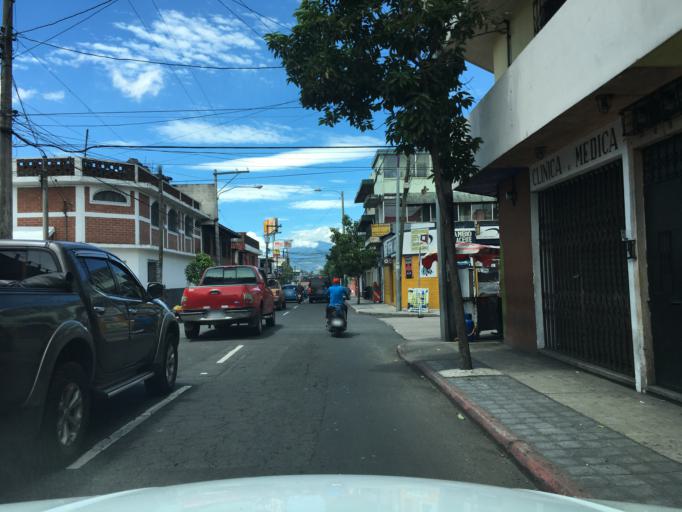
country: GT
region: Guatemala
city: Guatemala City
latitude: 14.6210
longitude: -90.5430
